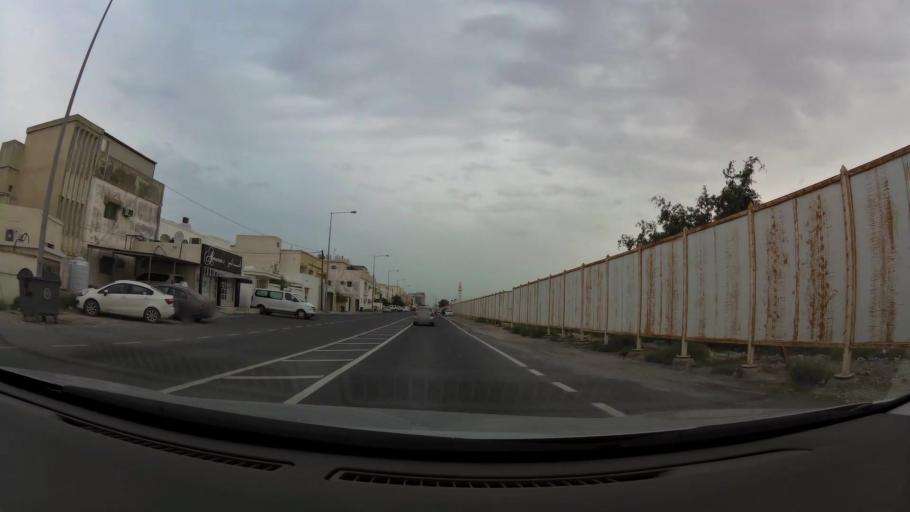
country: QA
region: Baladiyat ad Dawhah
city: Doha
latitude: 25.3192
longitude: 51.4905
